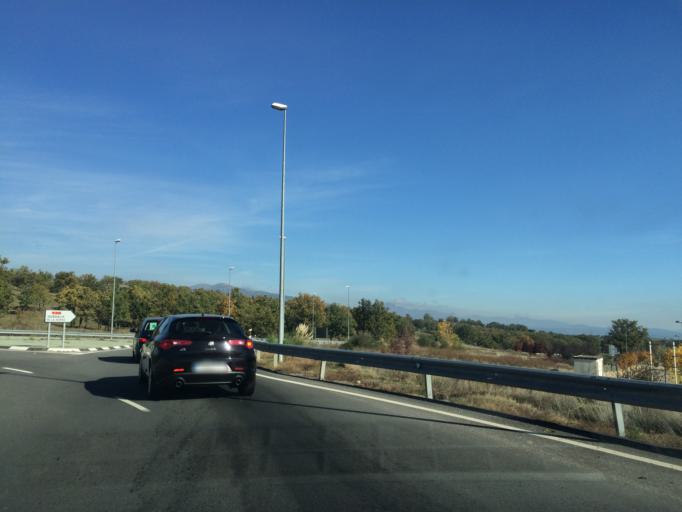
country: ES
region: Madrid
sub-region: Provincia de Madrid
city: Miraflores de la Sierra
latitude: 40.7647
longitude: -3.7477
